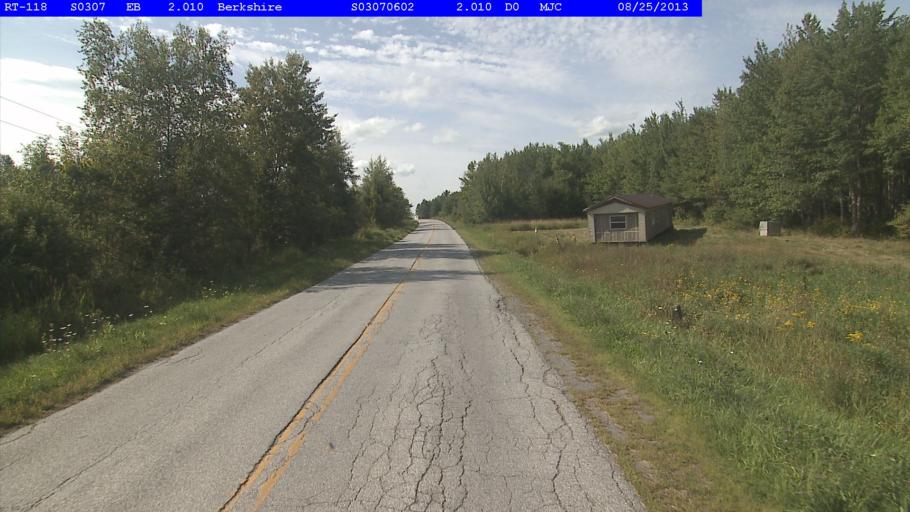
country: US
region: Vermont
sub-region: Franklin County
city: Enosburg Falls
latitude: 44.9479
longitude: -72.7440
